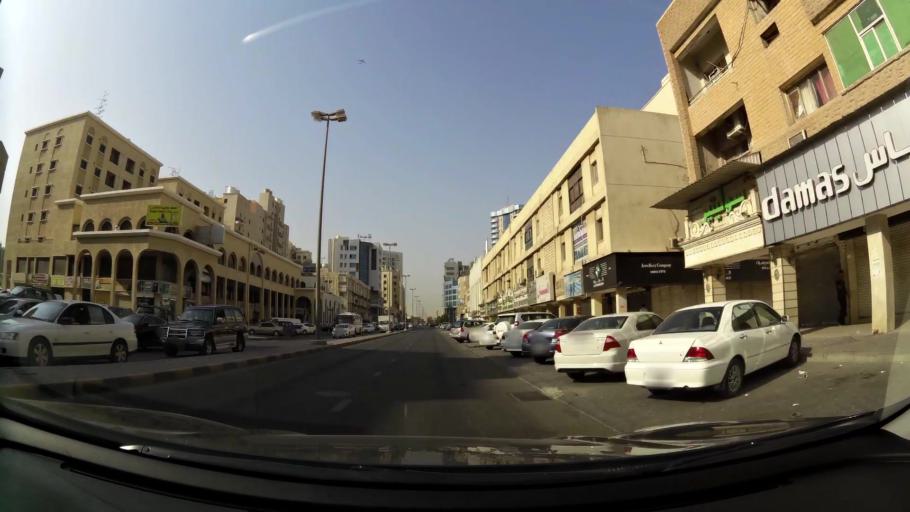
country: KW
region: Muhafazat Hawalli
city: Hawalli
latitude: 29.3408
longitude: 48.0090
